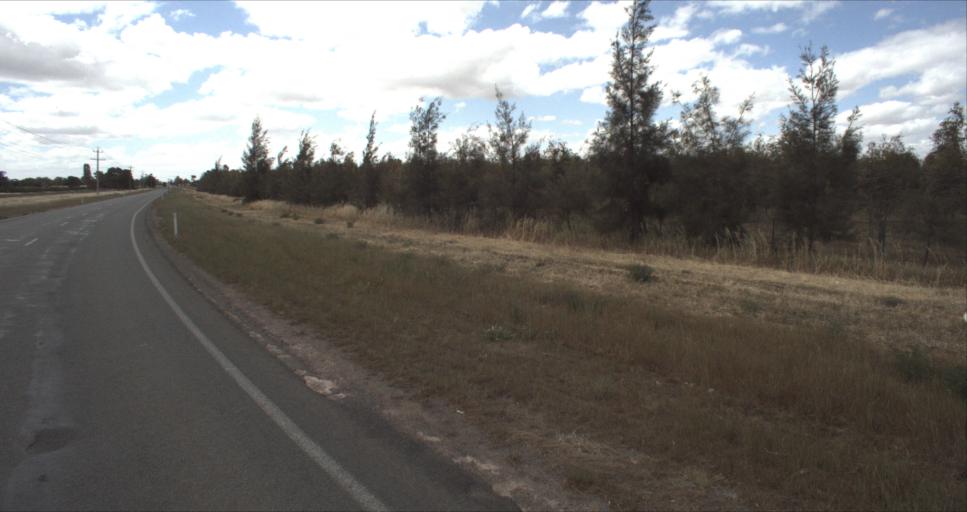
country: AU
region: New South Wales
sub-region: Leeton
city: Leeton
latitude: -34.5762
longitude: 146.3954
